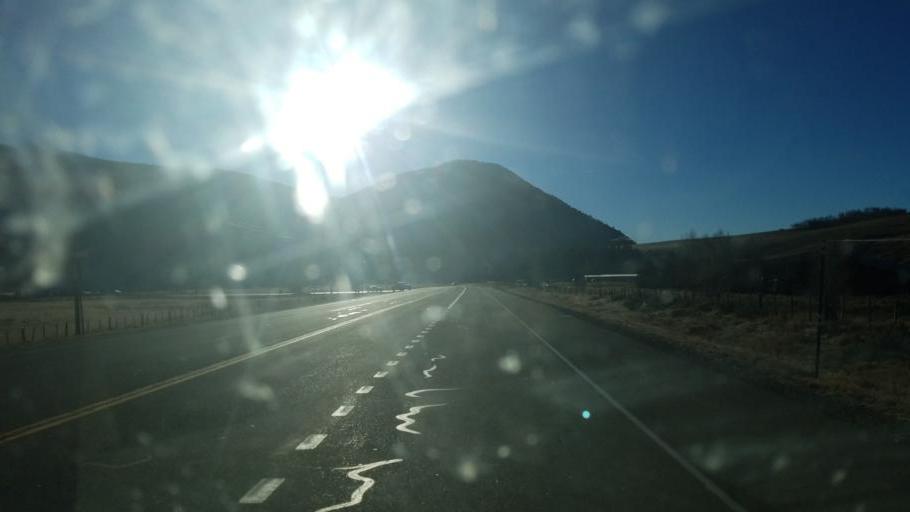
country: US
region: Colorado
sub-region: Gunnison County
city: Crested Butte
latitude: 38.8054
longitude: -106.8921
